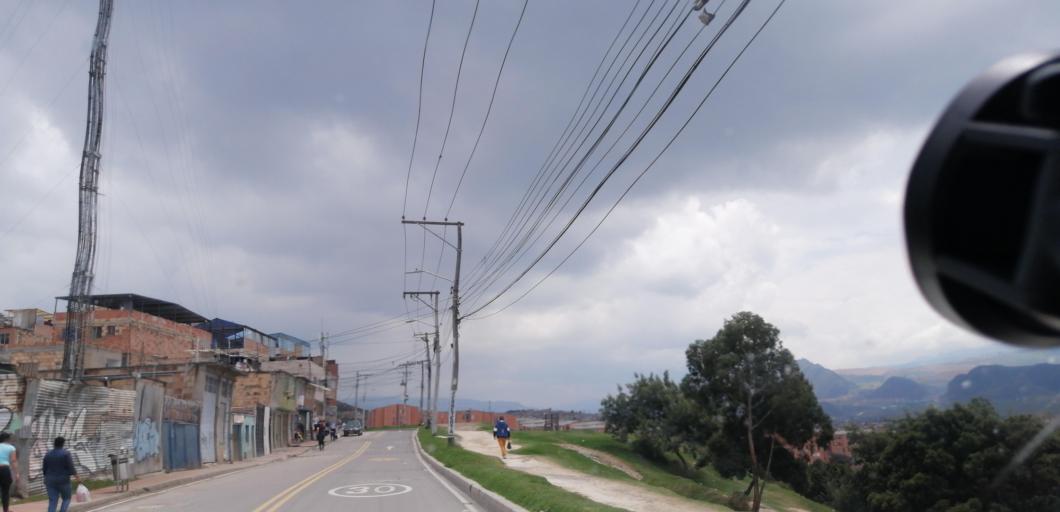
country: CO
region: Bogota D.C.
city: Bogota
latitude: 4.5342
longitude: -74.1156
